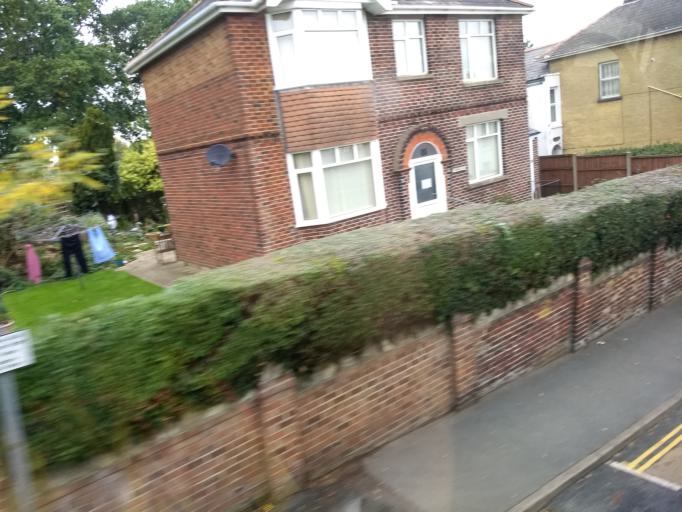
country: GB
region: England
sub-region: Isle of Wight
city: Ryde
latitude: 50.7290
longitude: -1.1662
